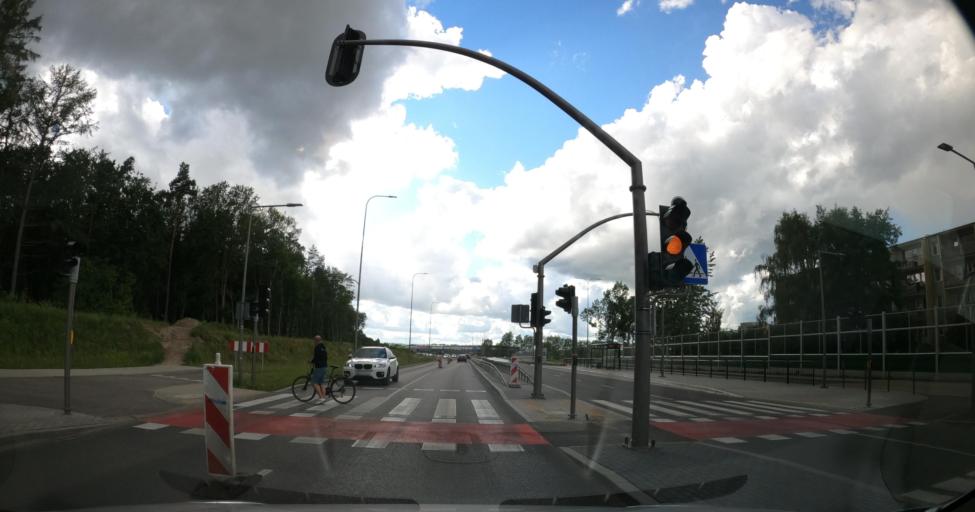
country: PL
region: Pomeranian Voivodeship
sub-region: Powiat gdanski
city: Lublewo Gdanskie
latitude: 54.3533
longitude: 18.4943
